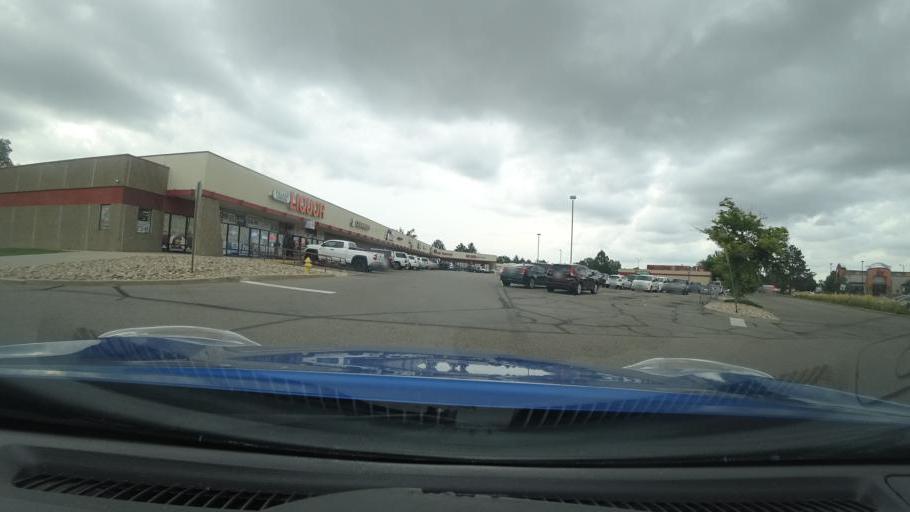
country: US
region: Colorado
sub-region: Adams County
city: Aurora
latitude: 39.6953
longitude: -104.8118
